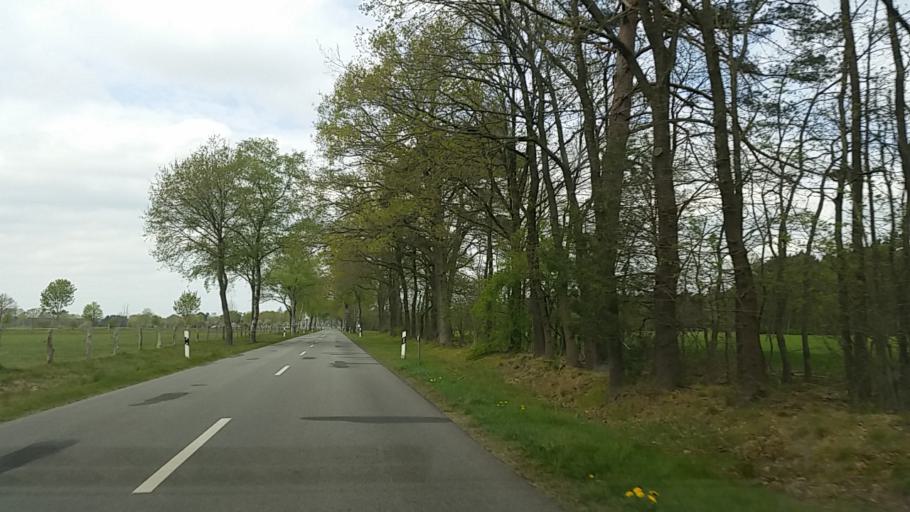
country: DE
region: Lower Saxony
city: Otter
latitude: 53.1912
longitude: 9.7329
